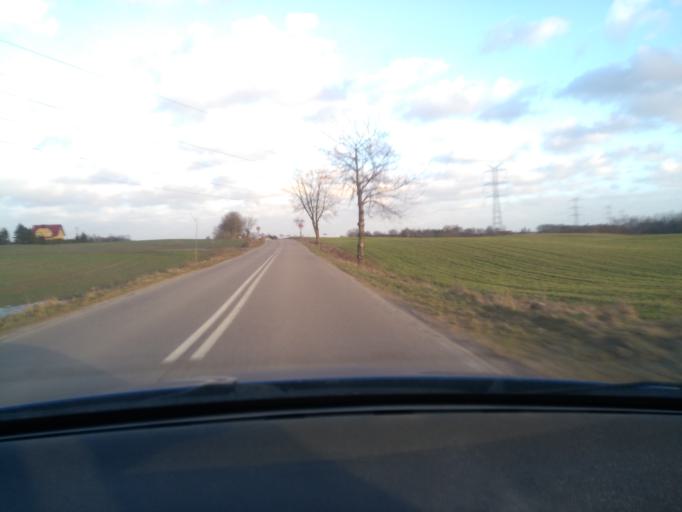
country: PL
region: Pomeranian Voivodeship
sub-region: Powiat kartuski
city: Przodkowo
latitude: 54.4169
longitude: 18.2949
